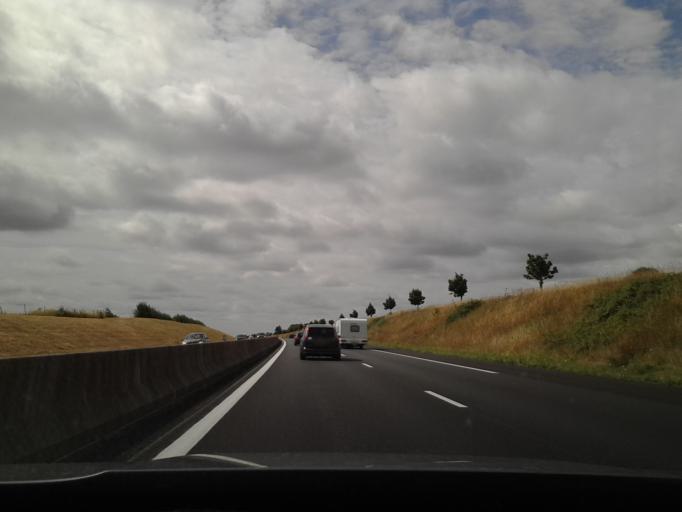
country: FR
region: Lower Normandy
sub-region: Departement de l'Orne
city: Sees
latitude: 48.5716
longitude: 0.1750
